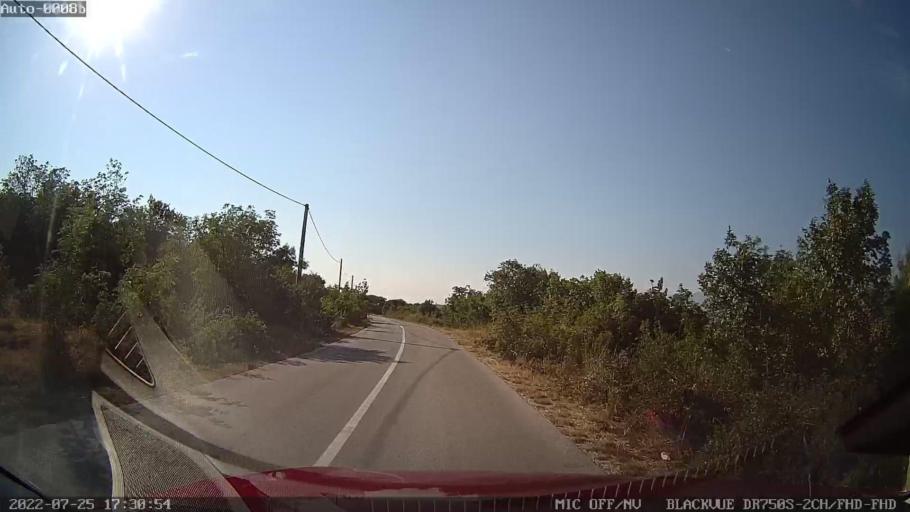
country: HR
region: Zadarska
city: Posedarje
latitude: 44.1670
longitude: 15.5044
